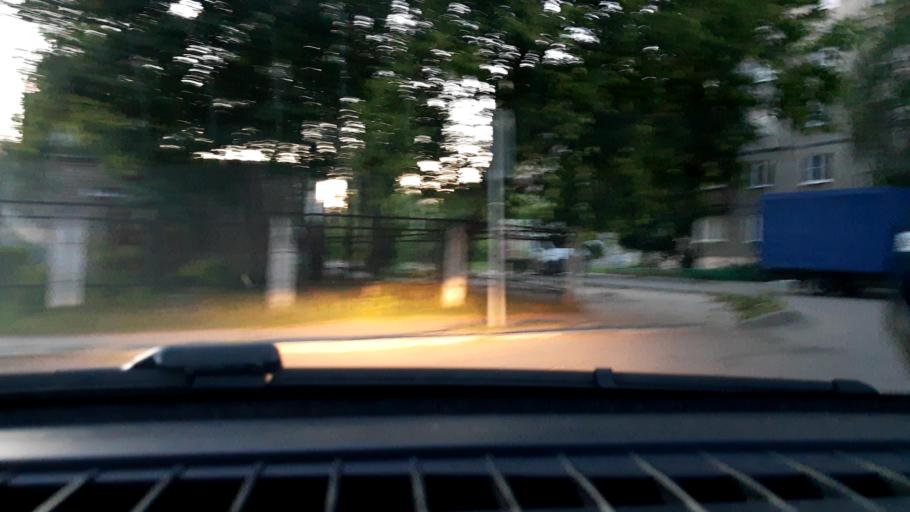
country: RU
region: Nizjnij Novgorod
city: Zavolzh'ye
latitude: 56.6315
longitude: 43.4074
